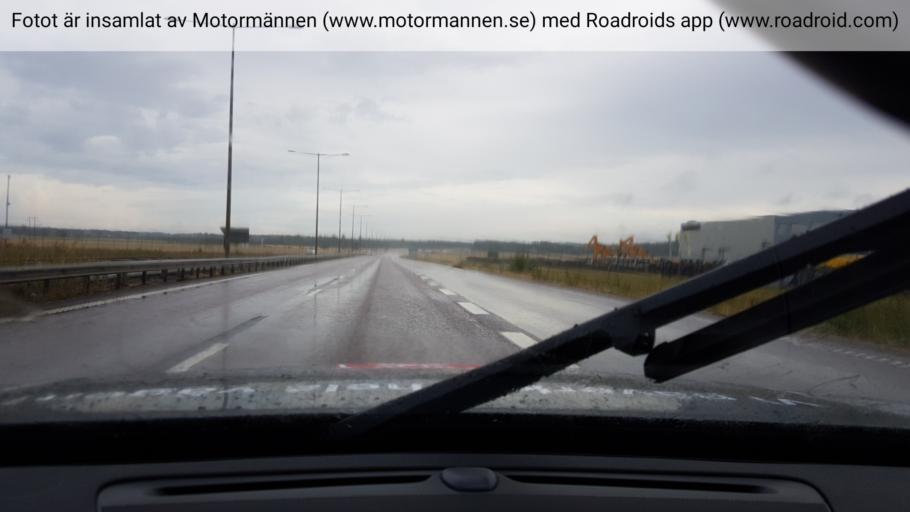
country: SE
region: Vaestmanland
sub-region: Vasteras
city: Tillberga
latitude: 59.6106
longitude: 16.6353
